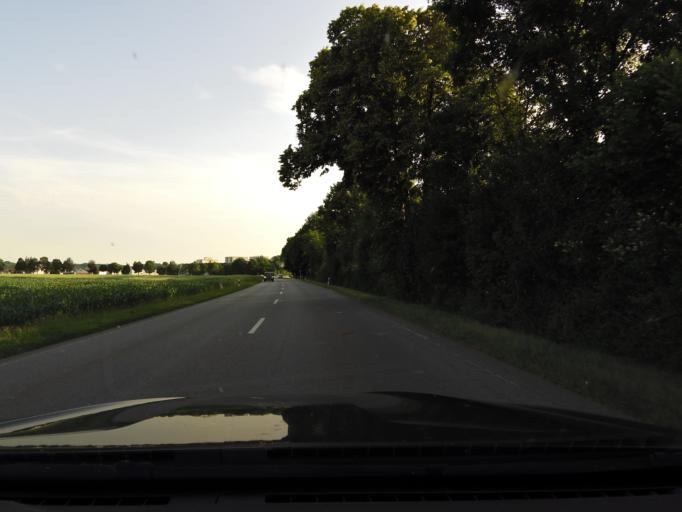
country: DE
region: Bavaria
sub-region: Upper Bavaria
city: Altoetting
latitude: 48.2332
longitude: 12.6650
